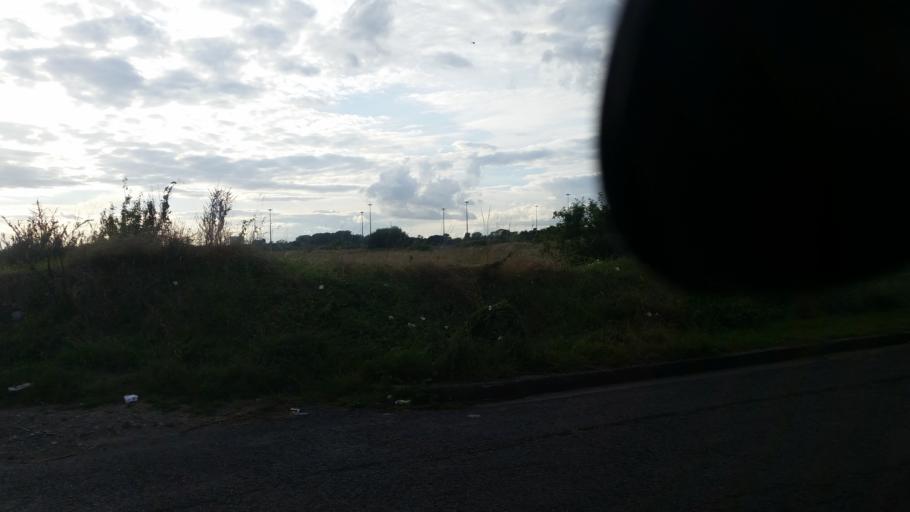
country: IE
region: Leinster
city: Beaumont
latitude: 53.3946
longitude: -6.2341
